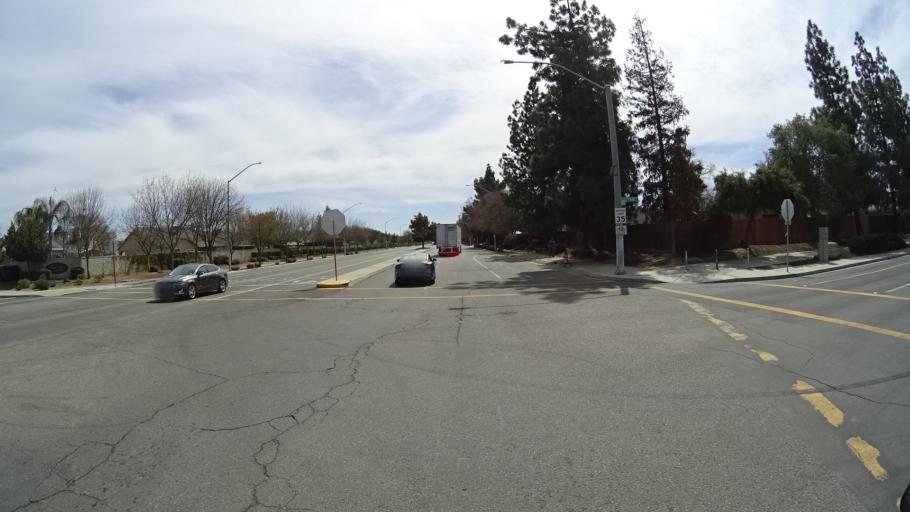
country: US
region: California
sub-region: Fresno County
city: West Park
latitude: 36.8009
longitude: -119.8896
